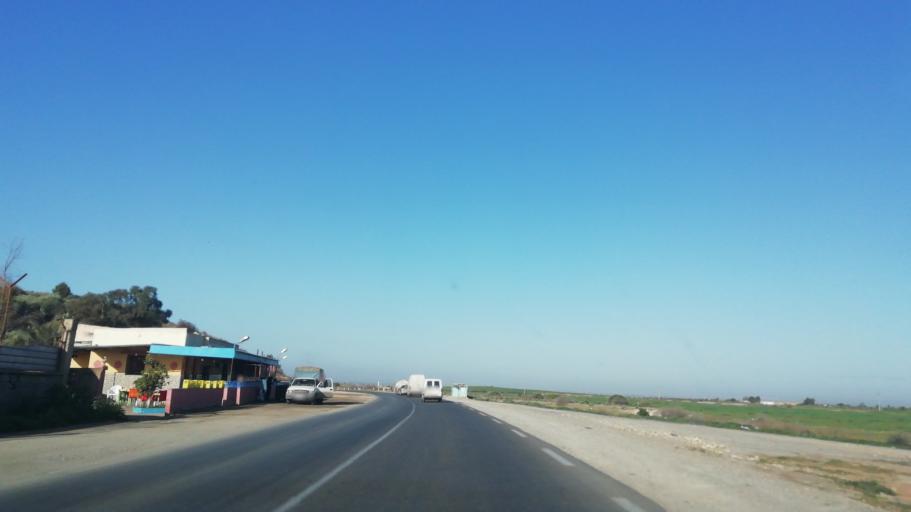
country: DZ
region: Mascara
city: Mascara
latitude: 35.6504
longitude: 0.1750
